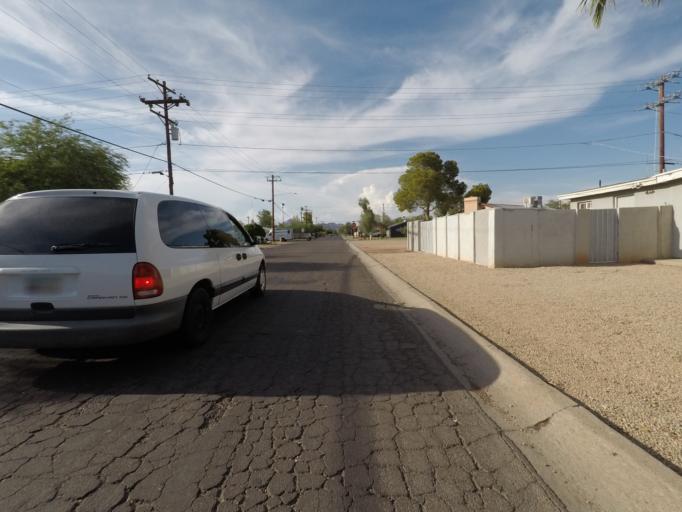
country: US
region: Arizona
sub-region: Maricopa County
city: Phoenix
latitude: 33.4725
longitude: -112.0085
